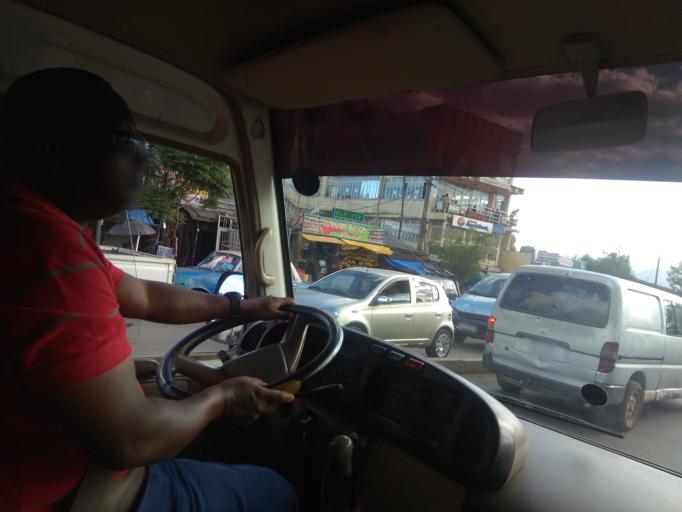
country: ET
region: Adis Abeba
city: Addis Ababa
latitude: 9.0337
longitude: 38.7140
